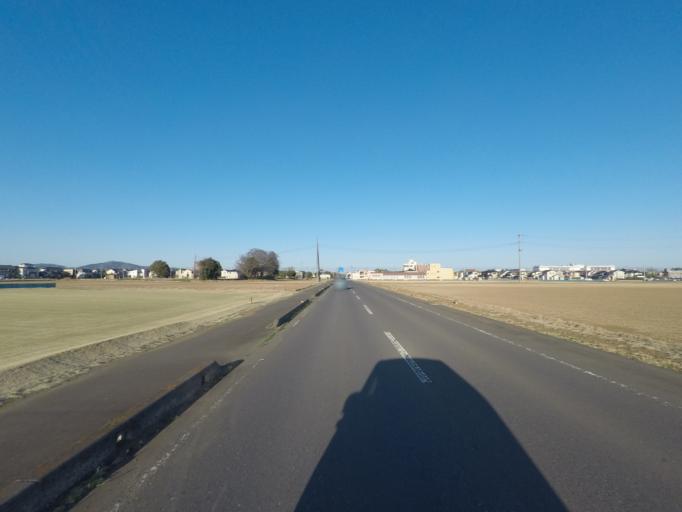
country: JP
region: Ibaraki
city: Ishige
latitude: 36.0945
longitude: 140.0624
